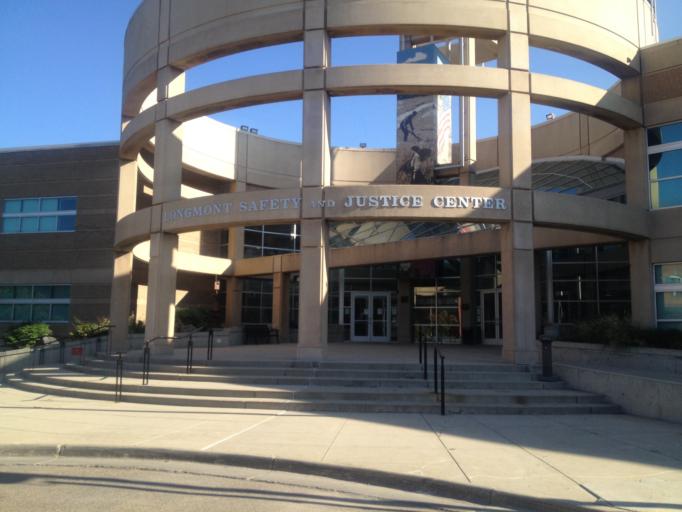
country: US
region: Colorado
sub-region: Boulder County
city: Longmont
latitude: 40.1634
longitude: -105.1012
